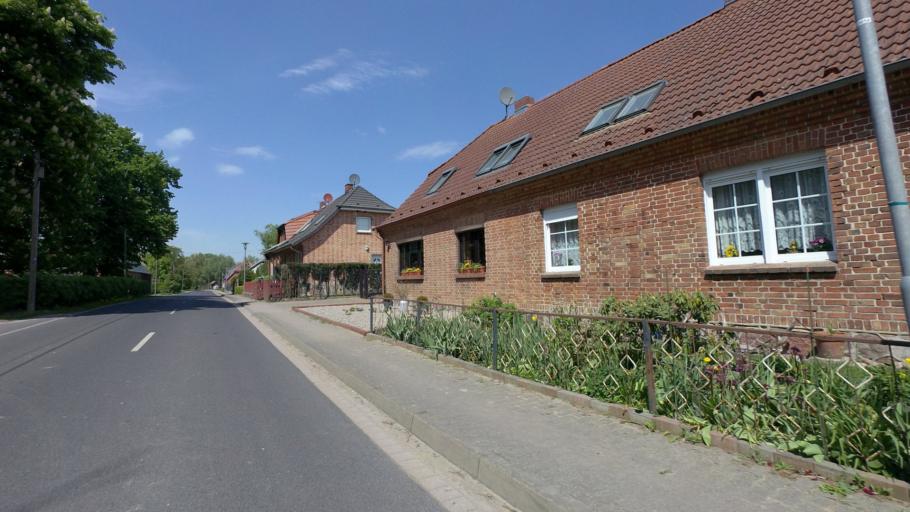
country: DE
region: Mecklenburg-Vorpommern
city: Mollenhagen
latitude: 53.5792
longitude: 12.8925
